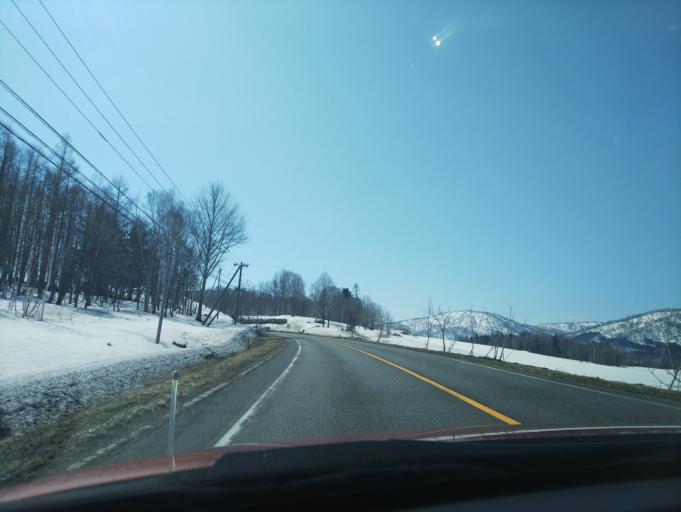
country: JP
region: Hokkaido
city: Nayoro
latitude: 44.6664
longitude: 142.2681
